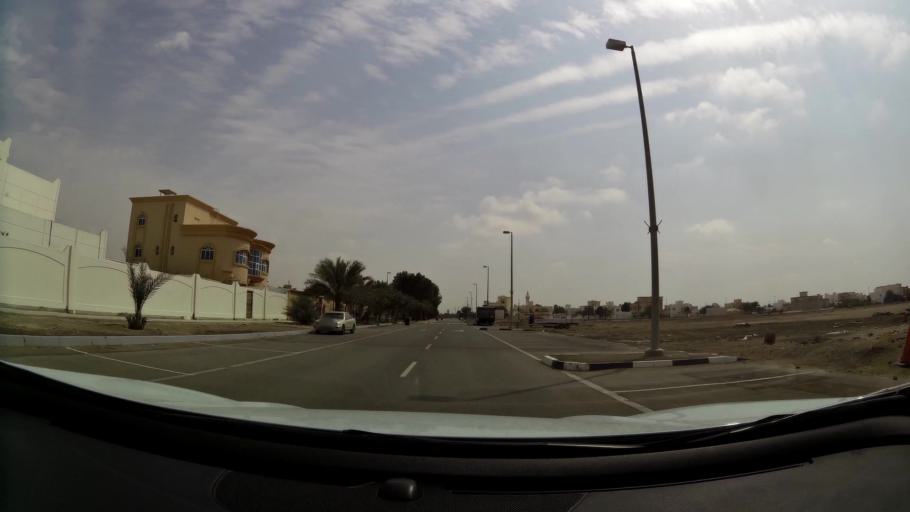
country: AE
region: Abu Dhabi
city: Abu Dhabi
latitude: 24.5506
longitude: 54.6346
